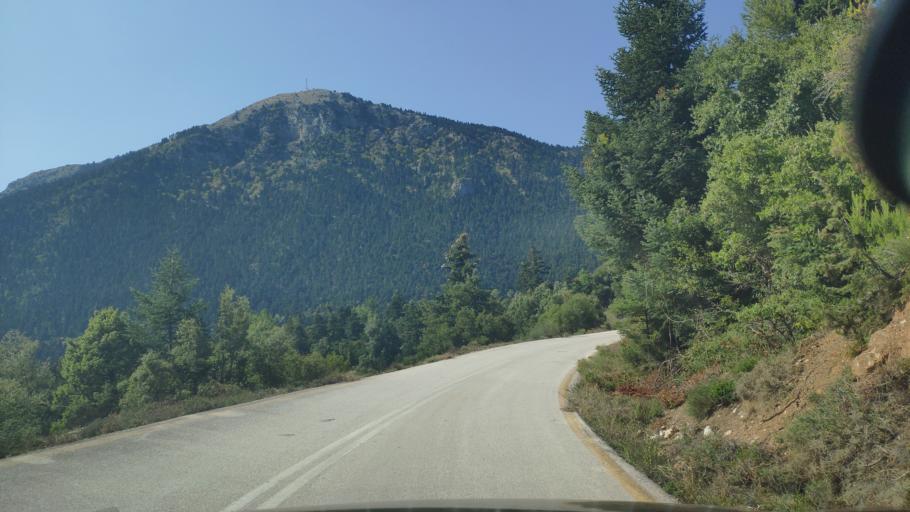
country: GR
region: Peloponnese
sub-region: Nomos Korinthias
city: Nemea
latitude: 37.8621
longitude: 22.3850
